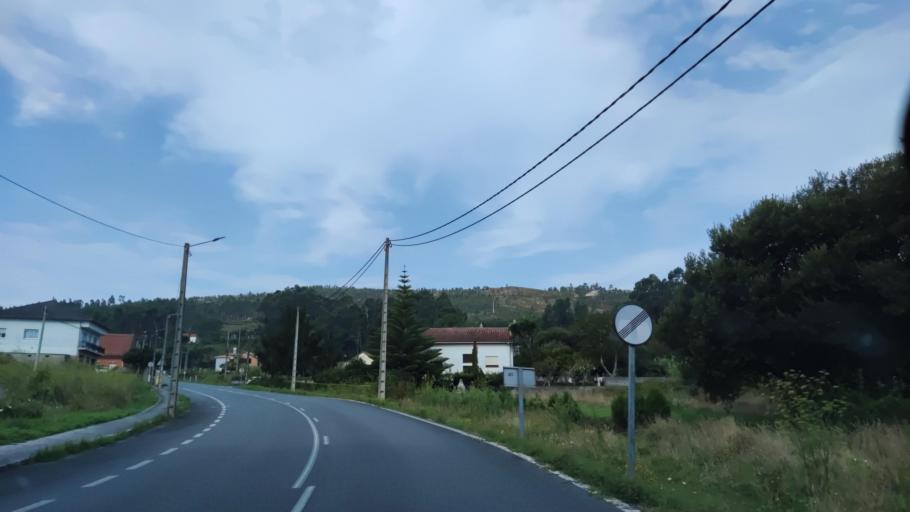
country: ES
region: Galicia
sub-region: Provincia da Coruna
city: Rianxo
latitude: 42.6543
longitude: -8.7723
